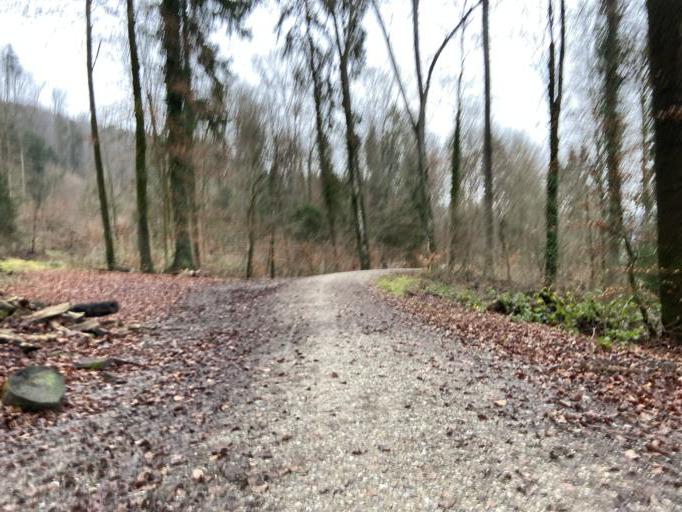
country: CH
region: Zurich
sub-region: Bezirk Winterthur
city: Toess (Kreis 4) / Vorder-Daettnau
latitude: 47.4835
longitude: 8.6887
